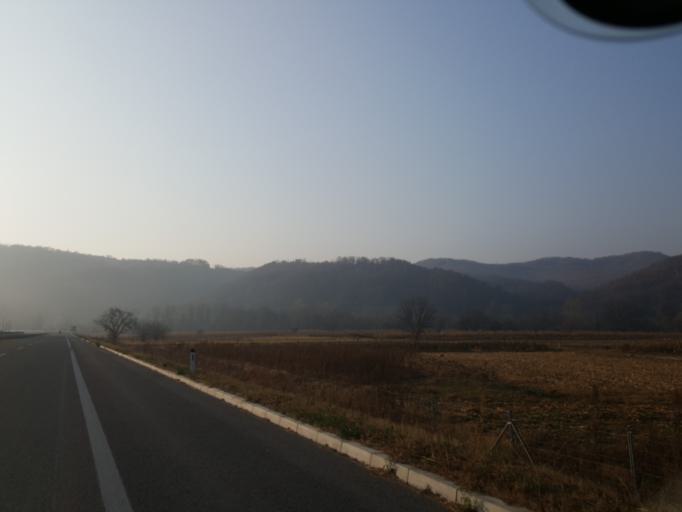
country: RS
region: Central Serbia
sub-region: Jablanicki Okrug
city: Vlasotince
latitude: 42.9029
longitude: 22.0502
